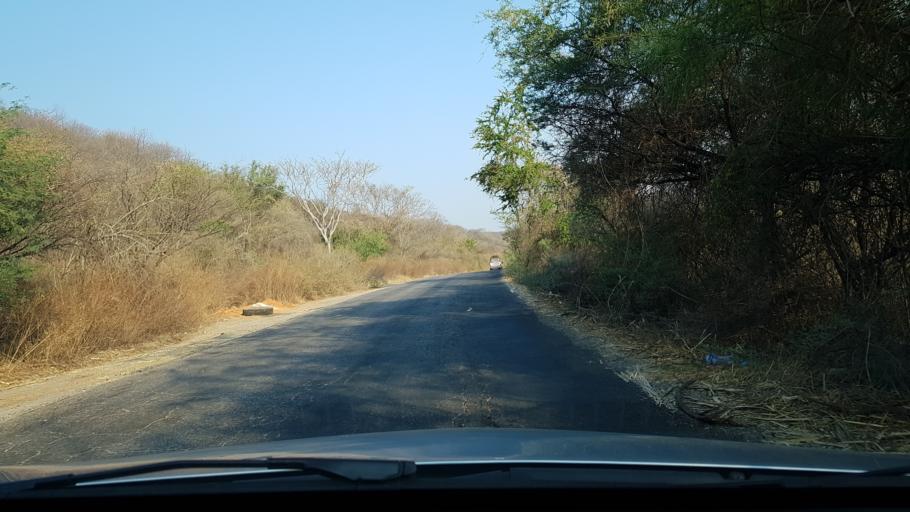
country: MX
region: Morelos
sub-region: Tepalcingo
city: Zacapalco
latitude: 18.6544
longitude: -99.0368
